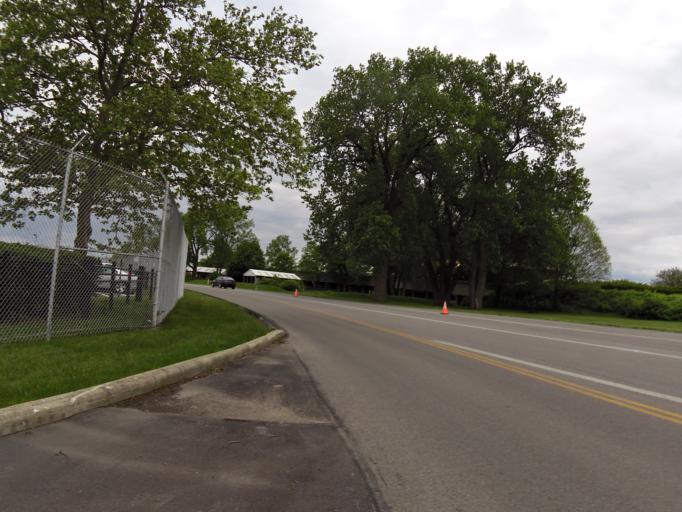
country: US
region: Ohio
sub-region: Franklin County
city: Columbus
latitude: 40.0032
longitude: -82.9876
